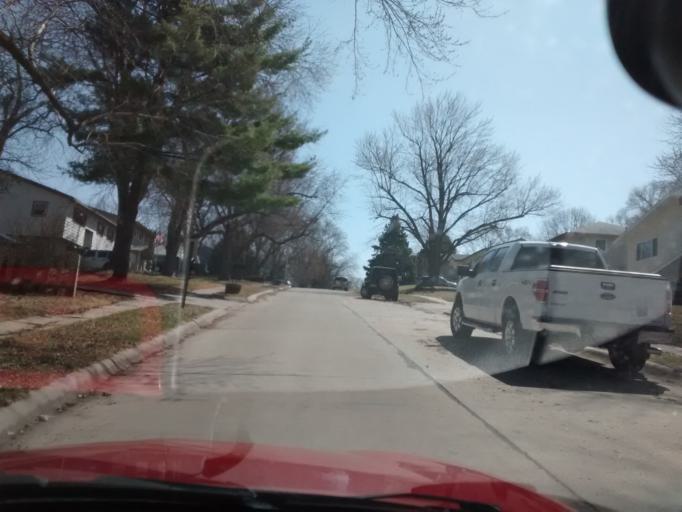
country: US
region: Nebraska
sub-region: Sarpy County
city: Bellevue
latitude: 41.1495
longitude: -95.9129
